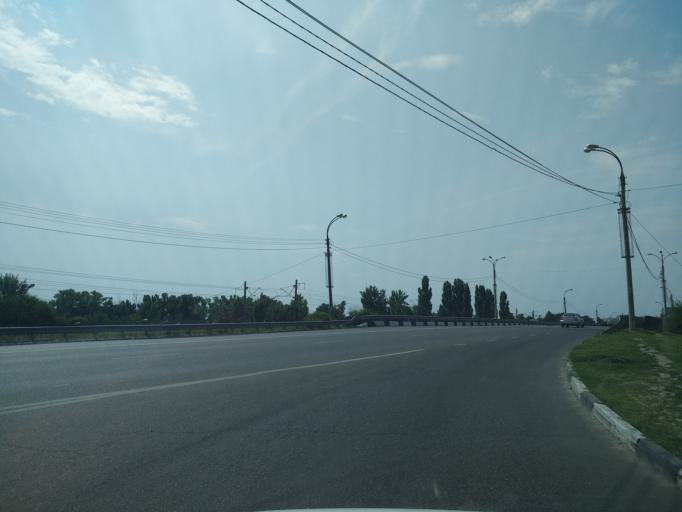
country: RU
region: Voronezj
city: Voronezh
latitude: 51.6957
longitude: 39.2283
